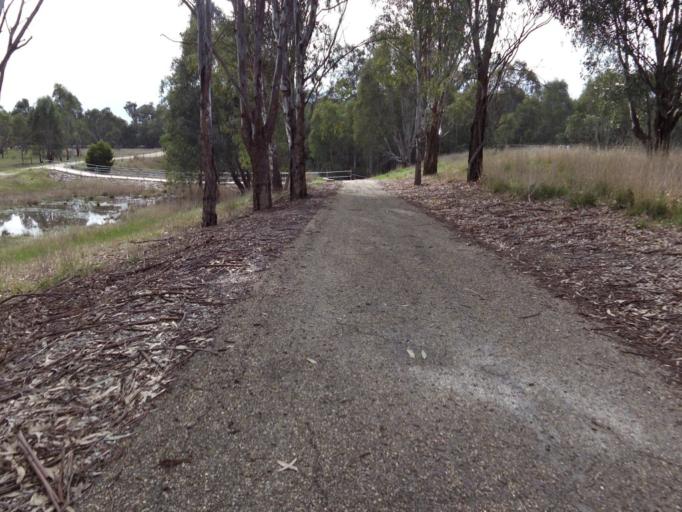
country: AU
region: Victoria
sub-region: Wangaratta
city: Wangaratta
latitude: -36.3939
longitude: 146.3432
